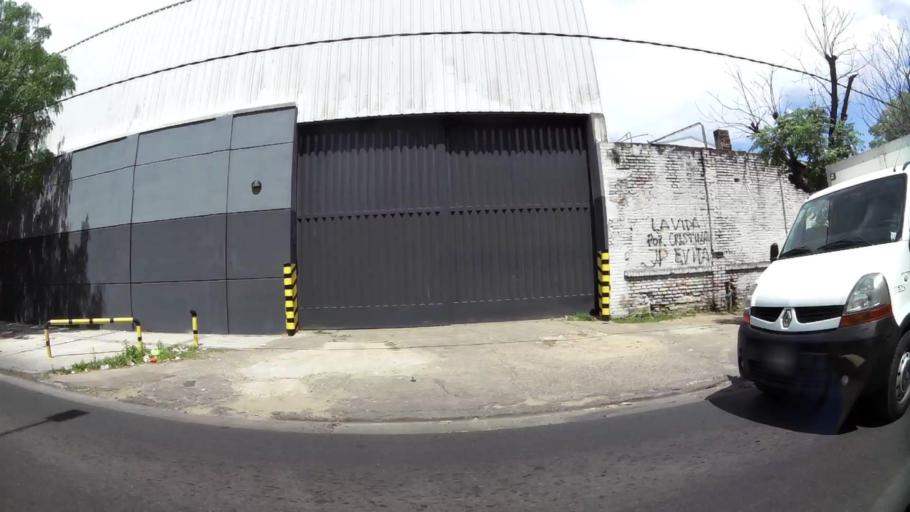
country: AR
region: Buenos Aires
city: San Justo
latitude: -34.6879
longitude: -58.5475
